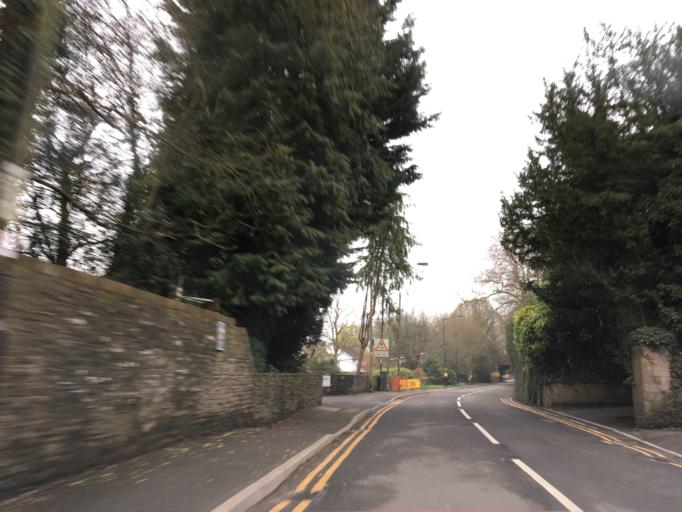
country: GB
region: Wales
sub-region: Monmouthshire
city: Usk
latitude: 51.7048
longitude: -2.9053
